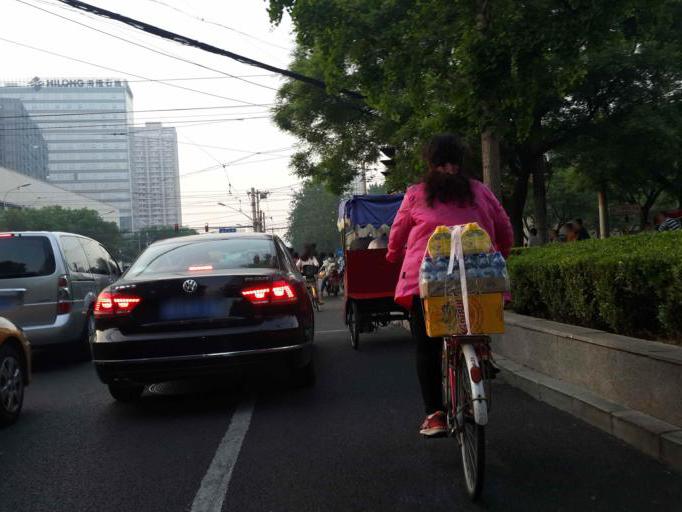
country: CN
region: Beijing
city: Chaowai
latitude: 39.9321
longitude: 116.4445
